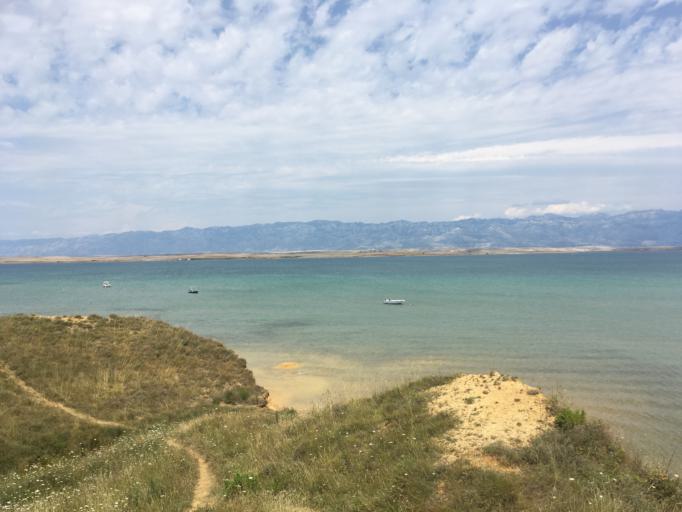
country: HR
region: Zadarska
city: Privlaka
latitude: 44.2712
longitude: 15.1504
